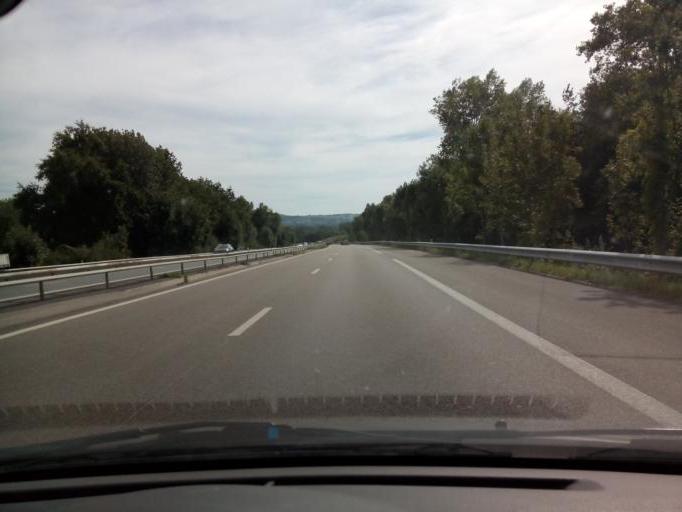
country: FR
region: Rhone-Alpes
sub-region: Departement de l'Isere
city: Saint-Victor-de-Cessieu
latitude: 45.5110
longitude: 5.4039
